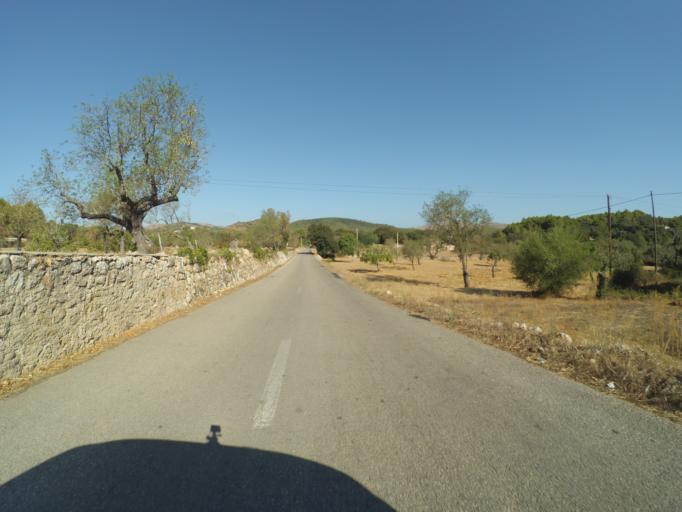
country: ES
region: Balearic Islands
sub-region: Illes Balears
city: Arta
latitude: 39.7004
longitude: 3.3510
